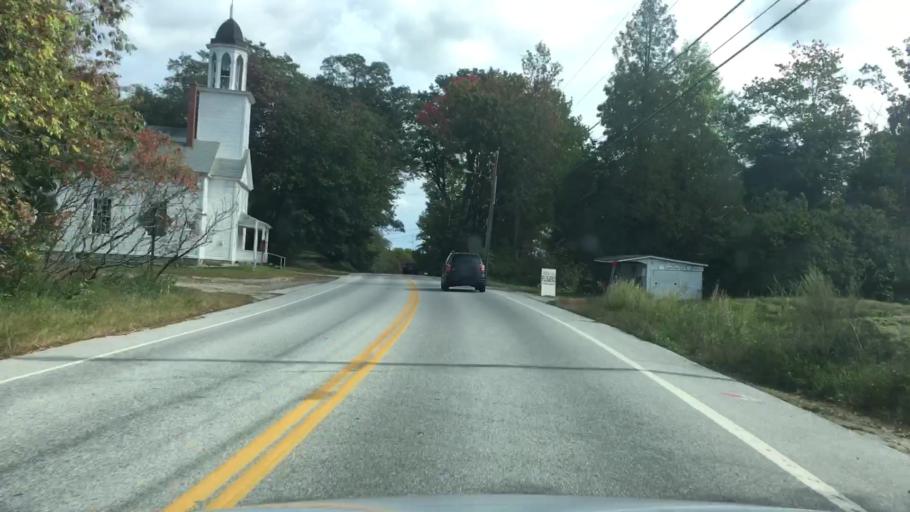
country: US
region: Maine
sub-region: Androscoggin County
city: Lisbon
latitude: 43.9817
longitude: -70.1294
